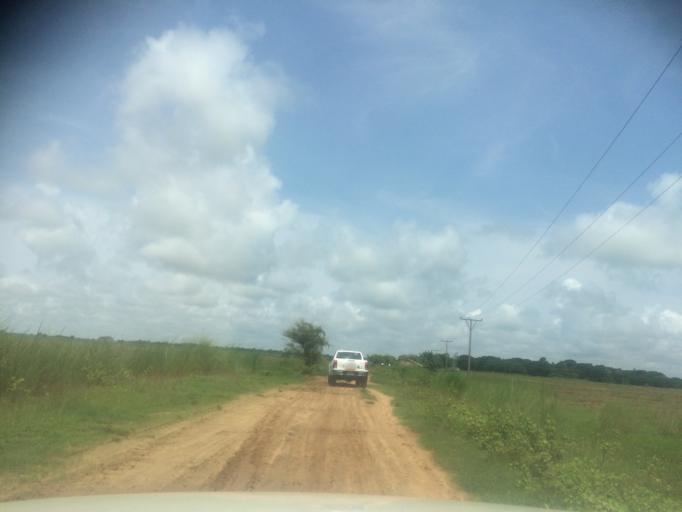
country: MM
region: Bago
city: Tharyarwady
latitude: 17.3176
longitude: 95.9024
